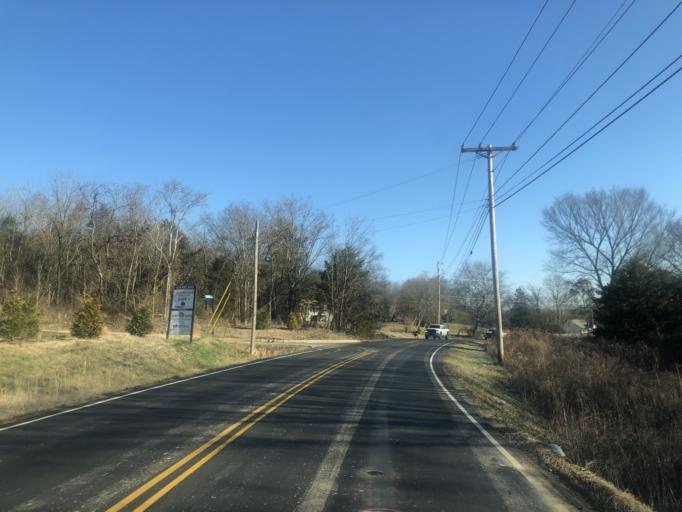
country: US
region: Tennessee
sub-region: Williamson County
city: Nolensville
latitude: 35.9666
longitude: -86.7003
